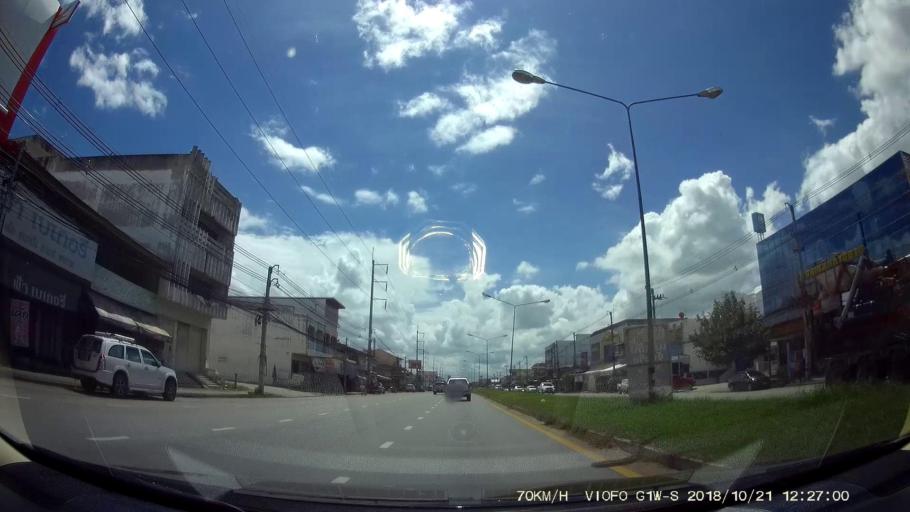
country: TH
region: Nakhon Ratchasima
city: Dan Khun Thot
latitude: 15.2059
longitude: 101.7661
